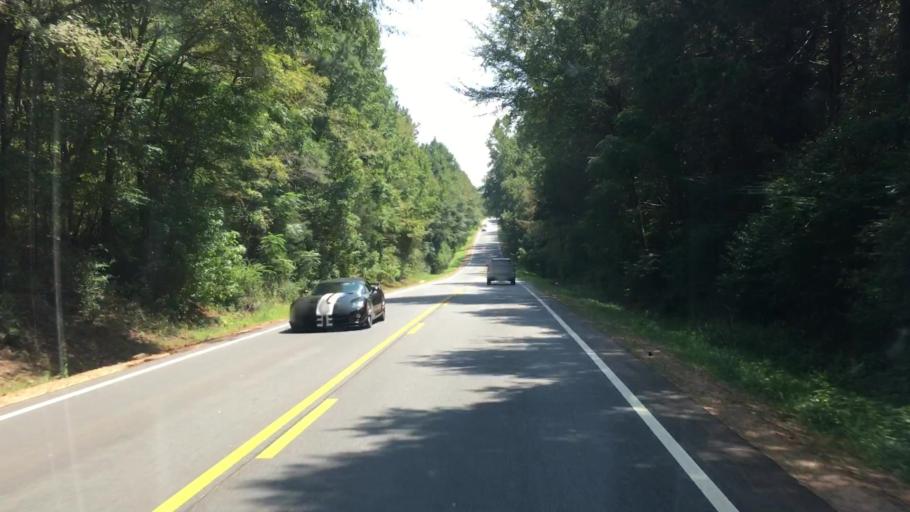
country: US
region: Georgia
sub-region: Oconee County
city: Watkinsville
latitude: 33.7903
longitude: -83.4245
